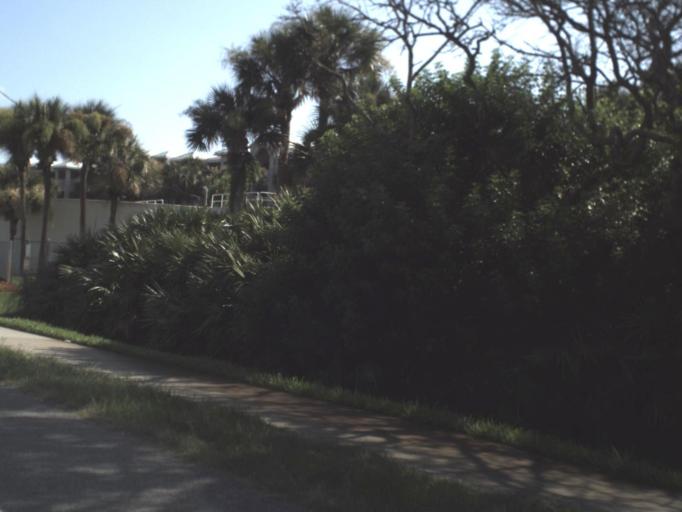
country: US
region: Florida
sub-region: Saint Johns County
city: Butler Beach
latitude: 29.7794
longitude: -81.2572
